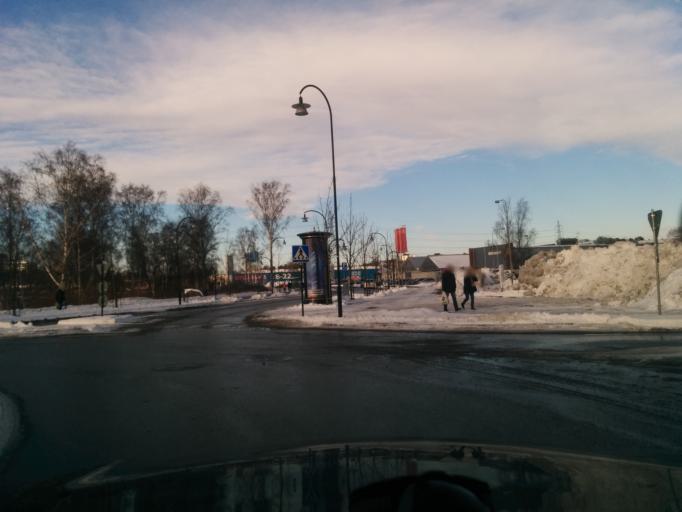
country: SE
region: Stockholm
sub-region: Sollentuna Kommun
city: Sollentuna
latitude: 59.4378
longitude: 17.9354
